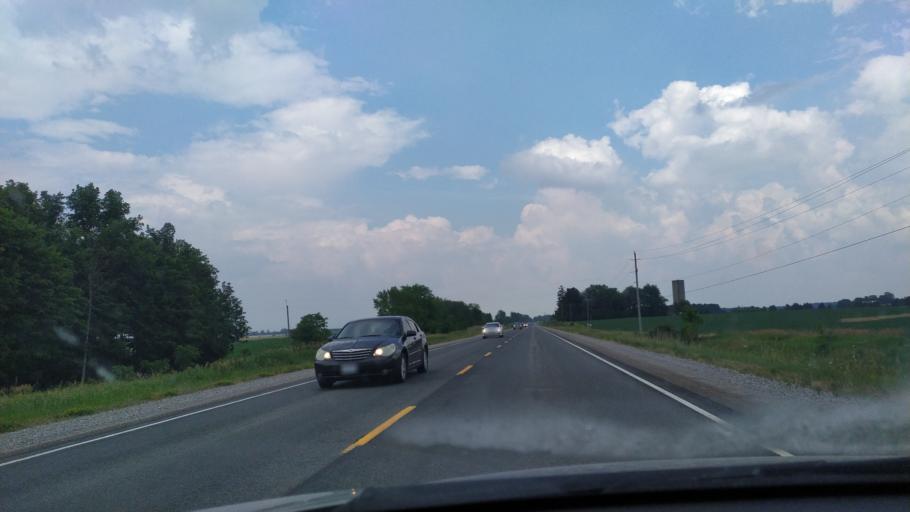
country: CA
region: Ontario
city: Stratford
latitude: 43.2368
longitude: -81.1148
